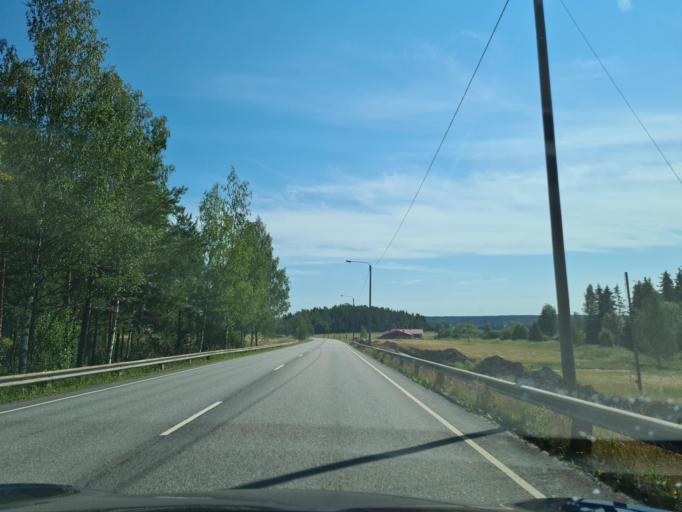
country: FI
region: Varsinais-Suomi
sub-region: Turku
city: Paimio
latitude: 60.4519
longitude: 22.6316
